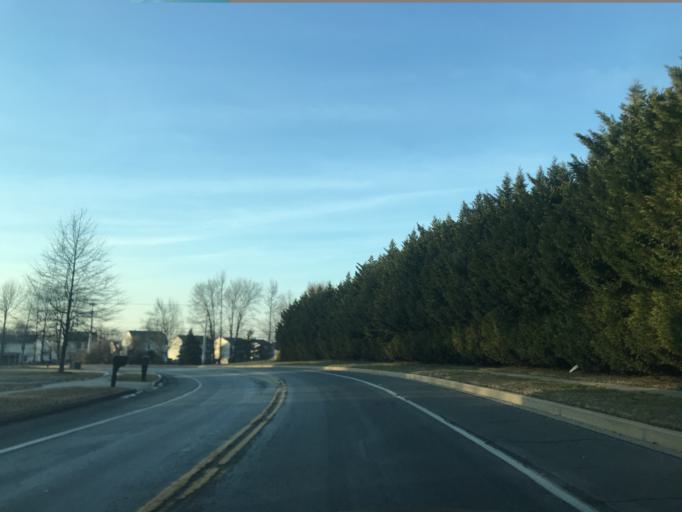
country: US
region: Maryland
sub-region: Harford County
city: Edgewood
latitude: 39.4335
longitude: -76.2709
